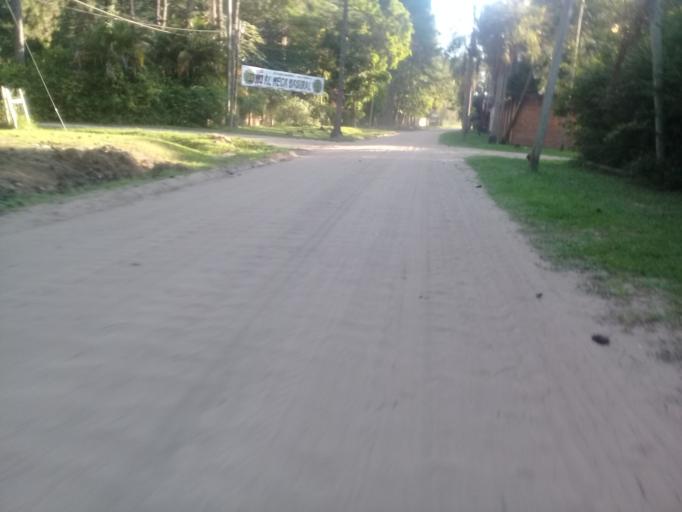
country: AR
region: Corrientes
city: San Luis del Palmar
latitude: -27.4624
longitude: -58.6656
